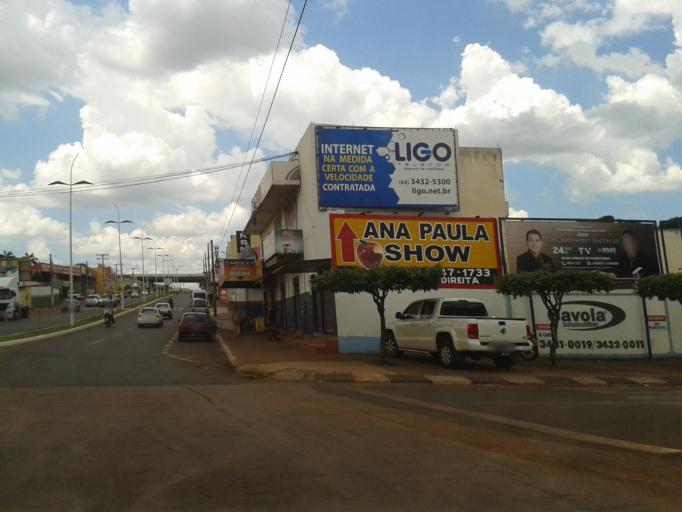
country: BR
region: Goias
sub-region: Itumbiara
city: Itumbiara
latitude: -18.4020
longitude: -49.2053
